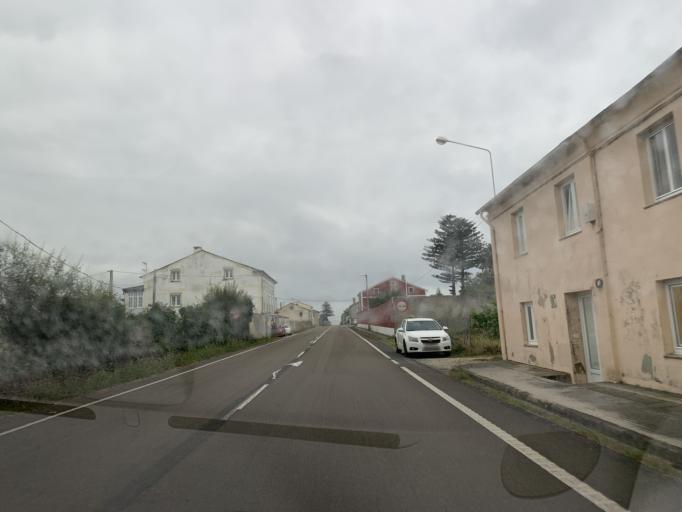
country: ES
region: Galicia
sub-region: Provincia de Lugo
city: Ribadeo
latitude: 43.5476
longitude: -7.1239
